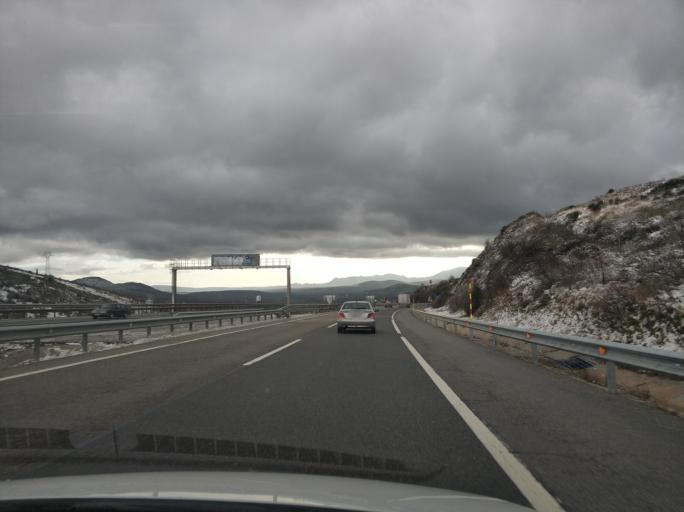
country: ES
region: Madrid
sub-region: Provincia de Madrid
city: Robregordo
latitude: 41.1146
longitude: -3.5874
